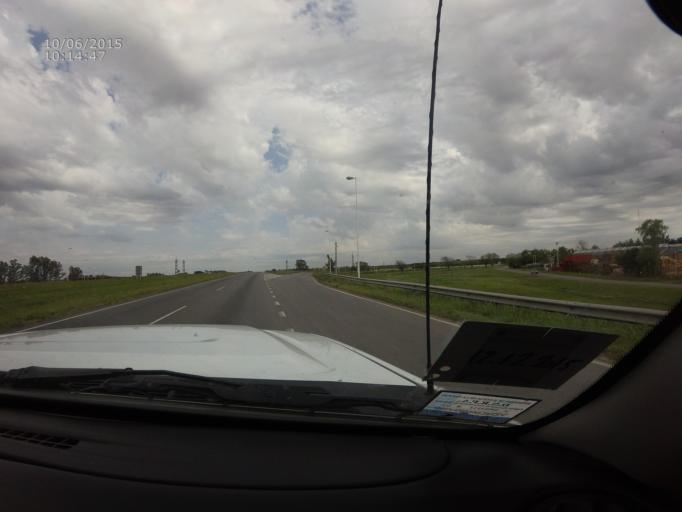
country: AR
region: Buenos Aires
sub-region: Partido de San Pedro
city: San Pedro
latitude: -33.7632
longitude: -59.7203
